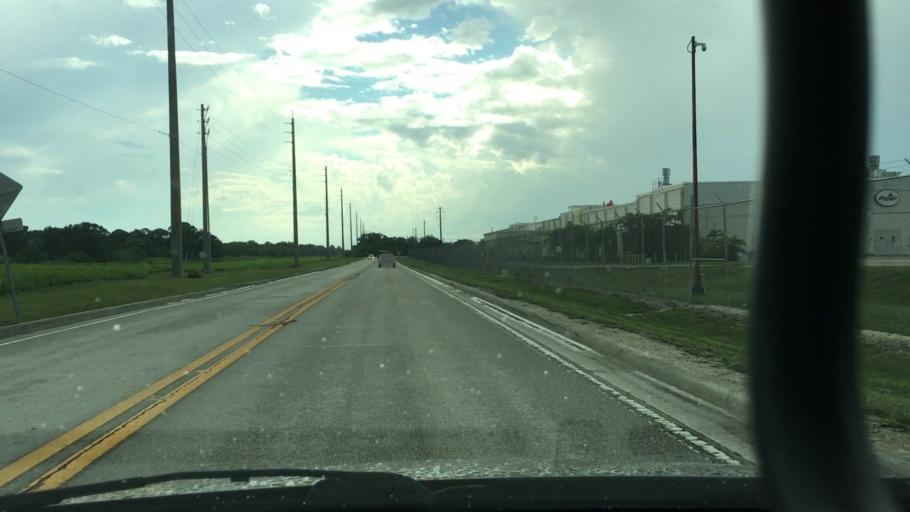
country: US
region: Florida
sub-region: Indian River County
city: Vero Beach
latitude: 27.6475
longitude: -80.4076
